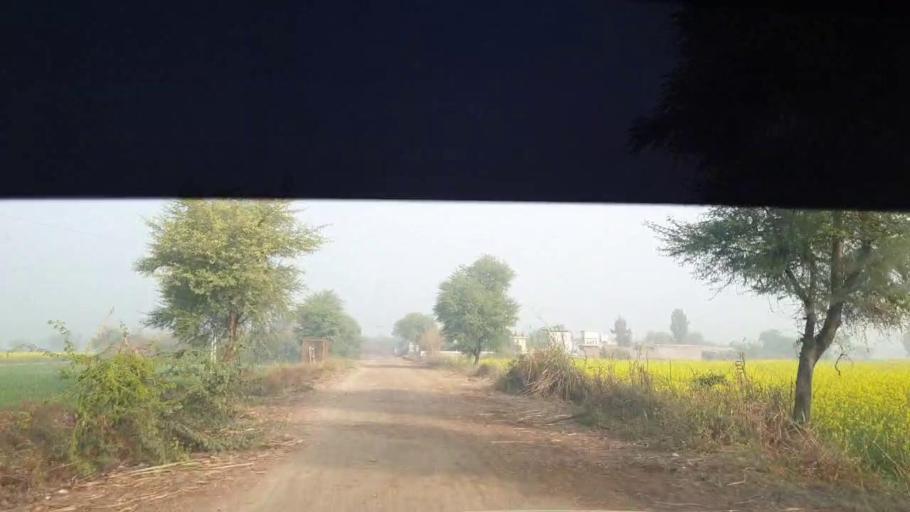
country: PK
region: Sindh
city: Berani
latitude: 25.7941
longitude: 68.7717
